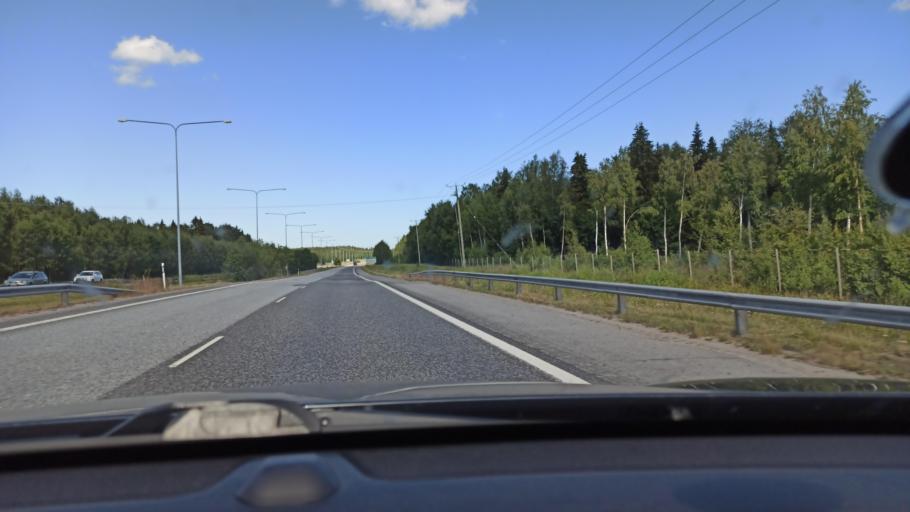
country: FI
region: Ostrobothnia
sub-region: Vaasa
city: Ristinummi
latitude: 63.0405
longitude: 21.7320
